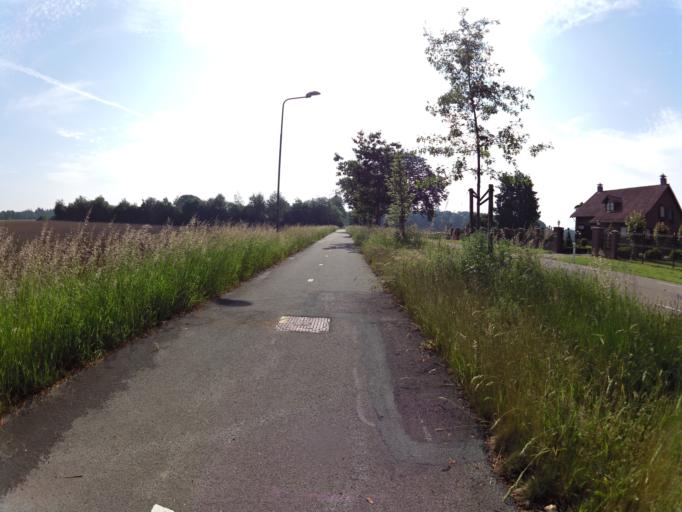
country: NL
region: Limburg
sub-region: Gemeente Echt-Susteren
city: Koningsbosch
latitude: 51.0831
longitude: 5.9387
